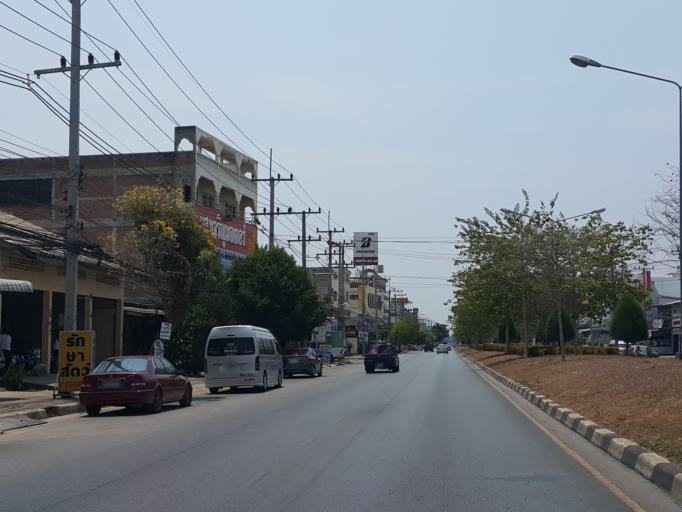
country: TH
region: Kanchanaburi
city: Kanchanaburi
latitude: 14.0390
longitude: 99.5180
